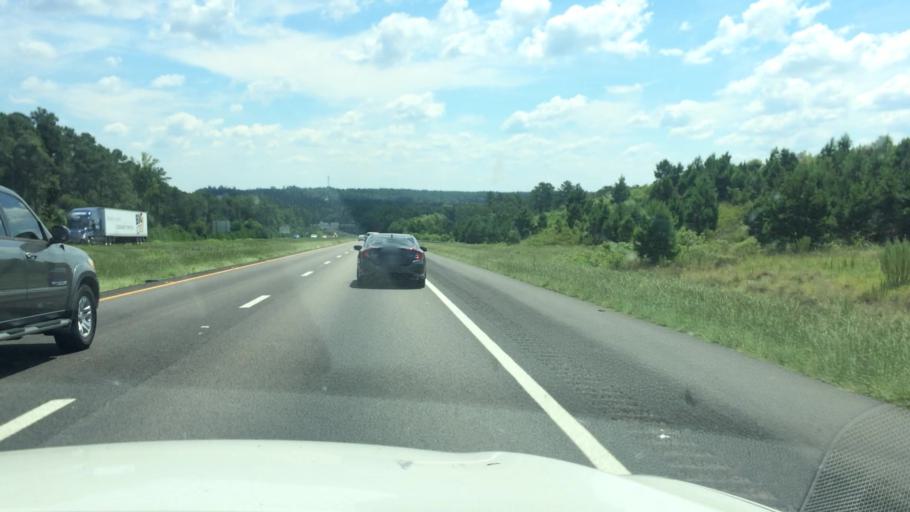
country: US
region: South Carolina
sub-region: Edgefield County
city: Murphys Estates
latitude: 33.5681
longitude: -81.9241
